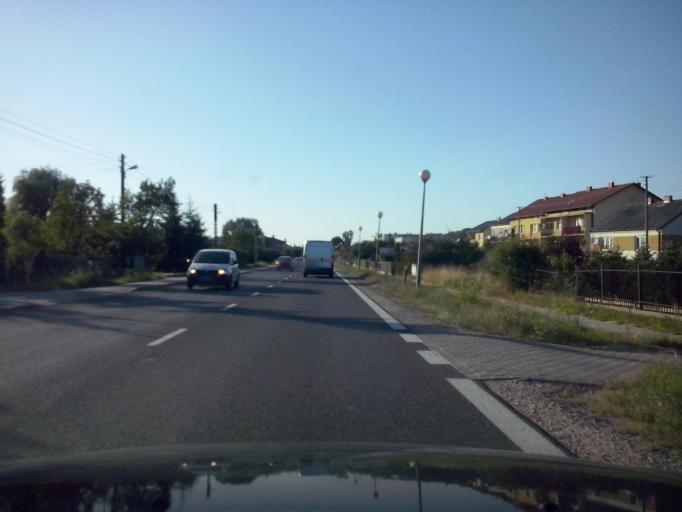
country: PL
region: Swietokrzyskie
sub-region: Powiat kielecki
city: Morawica
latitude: 50.7405
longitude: 20.6269
